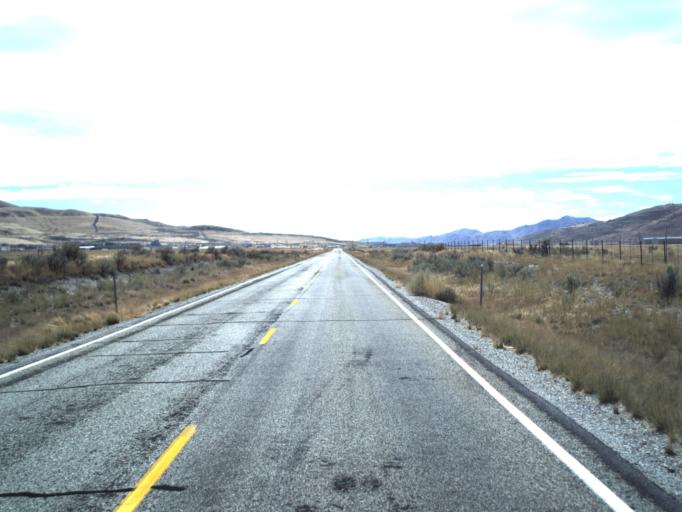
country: US
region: Utah
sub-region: Box Elder County
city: Tremonton
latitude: 41.7344
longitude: -112.4340
